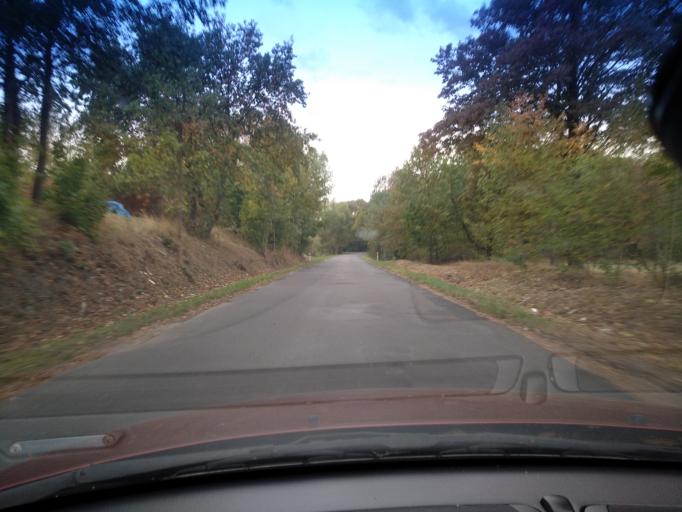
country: PL
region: Lower Silesian Voivodeship
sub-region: Powiat zgorzelecki
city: Zgorzelec
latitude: 51.1725
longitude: 15.0096
